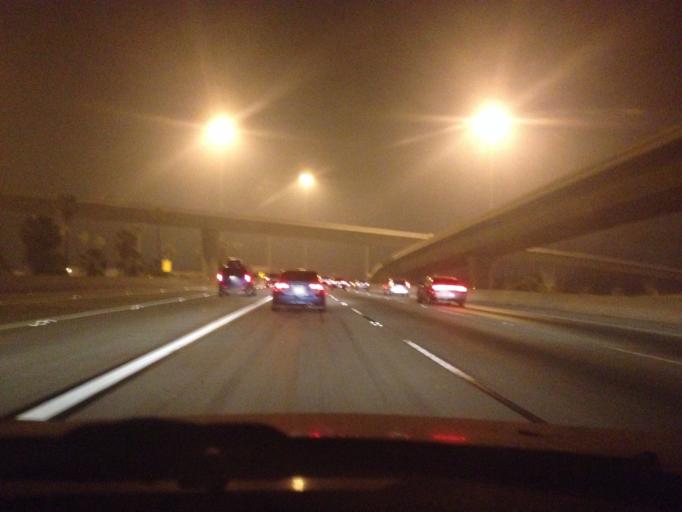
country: US
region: California
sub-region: Orange County
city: Buena Park
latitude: 33.8568
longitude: -117.9788
